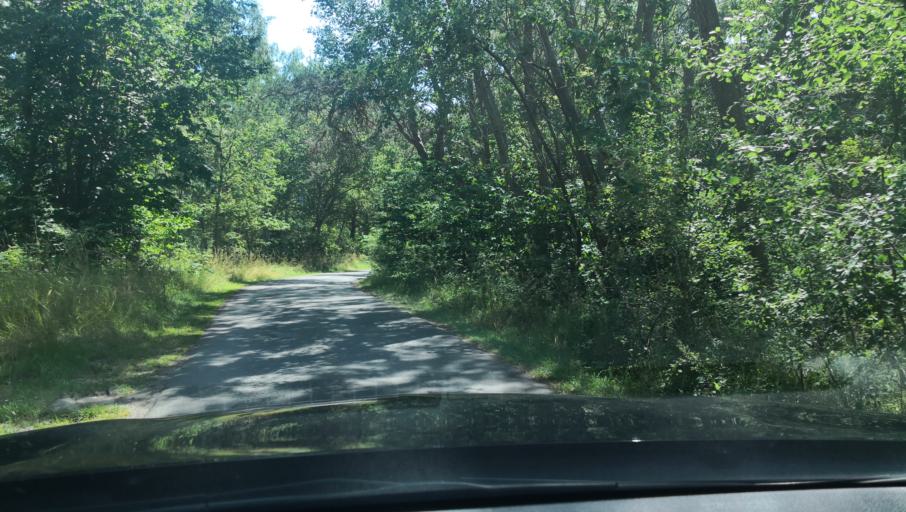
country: SE
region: Skane
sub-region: Ystads Kommun
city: Kopingebro
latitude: 55.3864
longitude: 14.1464
